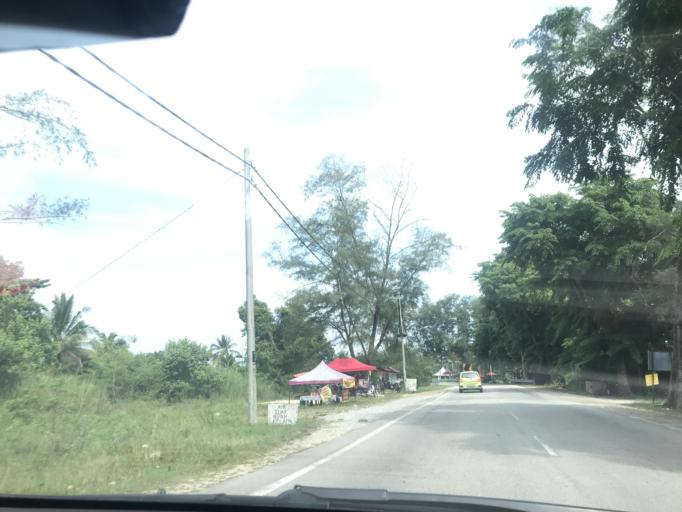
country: MY
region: Kelantan
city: Tumpat
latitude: 6.2062
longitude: 102.1461
